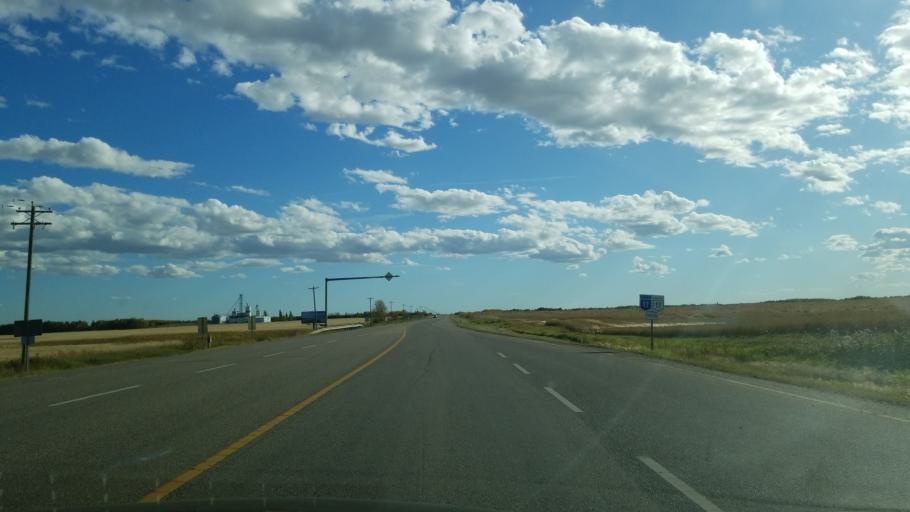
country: CA
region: Saskatchewan
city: Lloydminster
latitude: 53.2482
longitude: -110.0056
